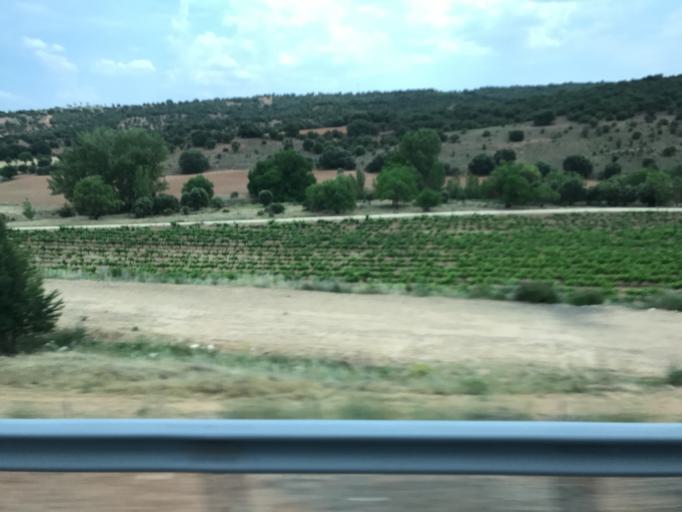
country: ES
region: Castille and Leon
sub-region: Provincia de Burgos
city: Pardilla
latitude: 41.5357
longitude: -3.7152
